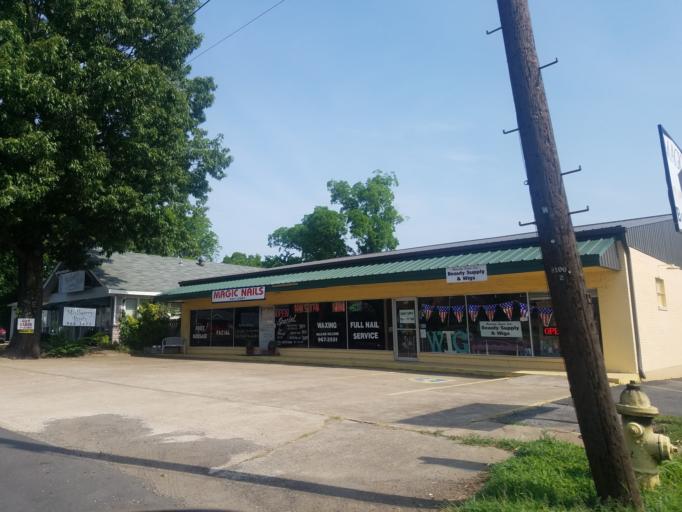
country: US
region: Arkansas
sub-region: Pope County
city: Russellville
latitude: 35.2792
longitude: -93.1371
